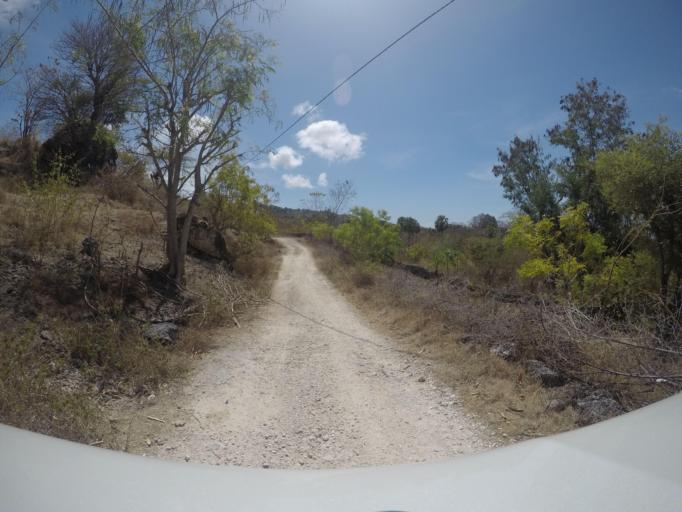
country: TL
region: Baucau
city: Baucau
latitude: -8.4447
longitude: 126.4392
